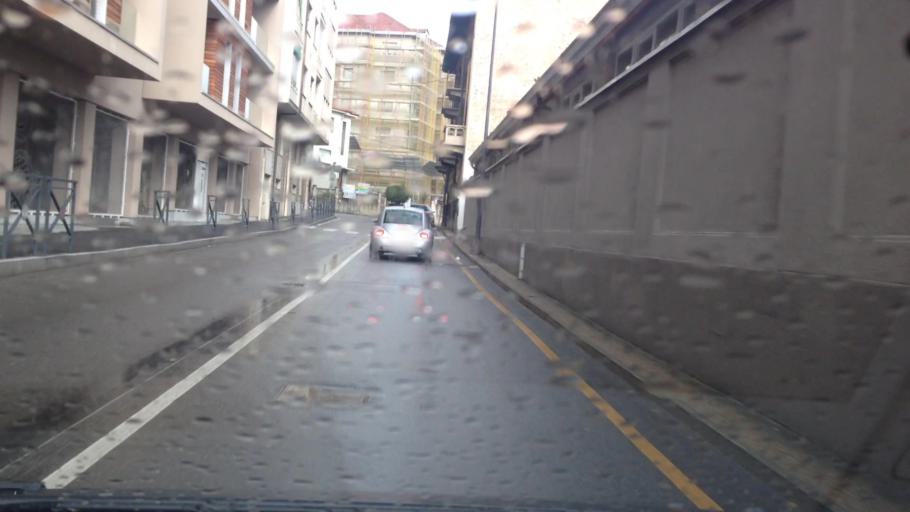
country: IT
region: Piedmont
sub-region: Provincia di Asti
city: Asti
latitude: 44.9041
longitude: 8.2104
